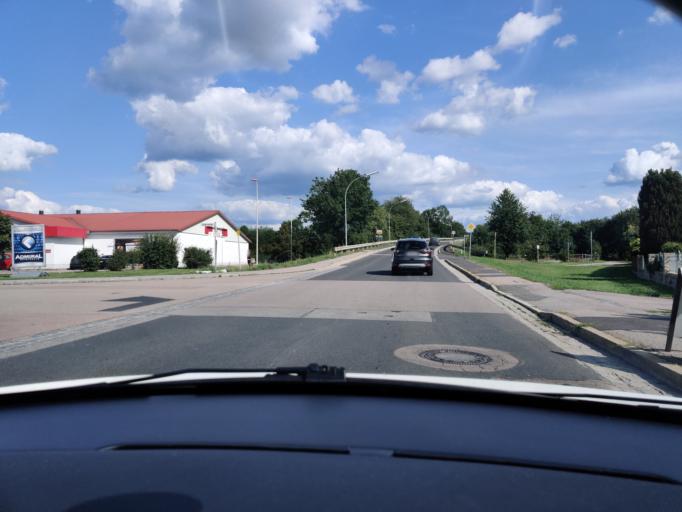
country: DE
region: Bavaria
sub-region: Upper Palatinate
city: Nabburg
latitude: 49.4522
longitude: 12.1903
